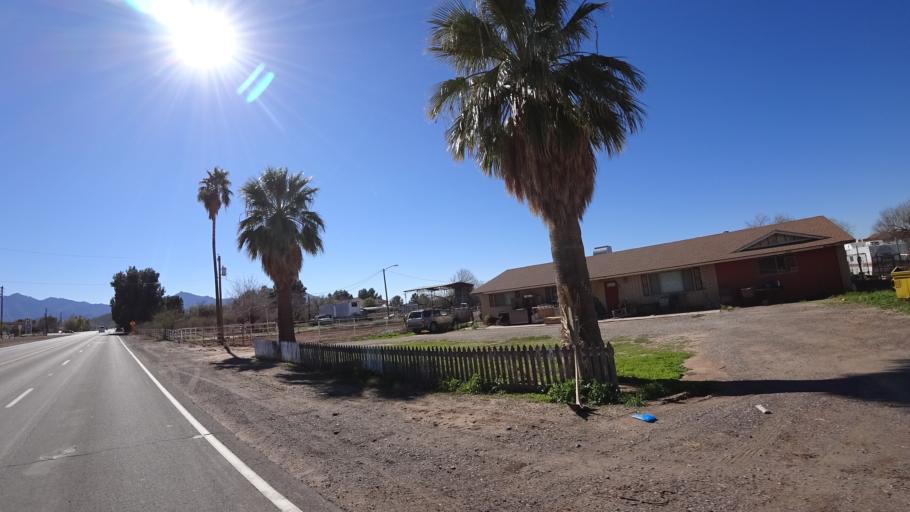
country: US
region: Arizona
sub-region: Maricopa County
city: Avondale
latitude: 33.3941
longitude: -112.3062
